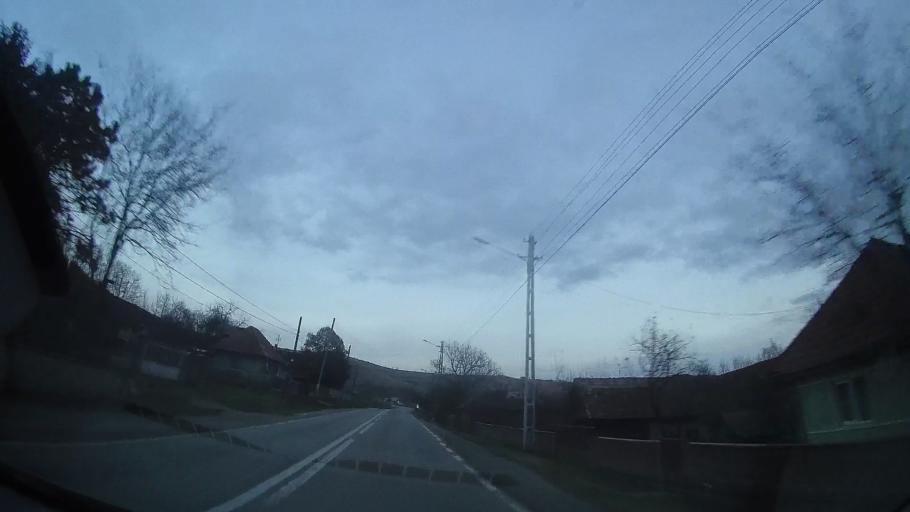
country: RO
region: Cluj
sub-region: Comuna Caianu
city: Vaida-Camaras
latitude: 46.8049
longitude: 23.9791
